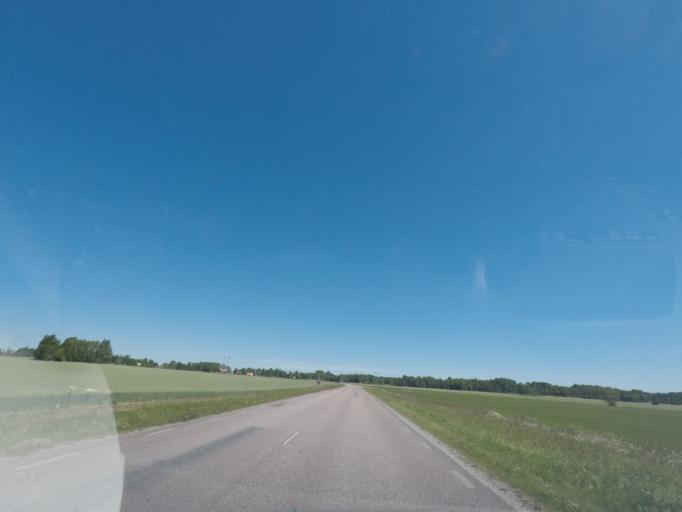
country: SE
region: Vaestmanland
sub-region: Vasteras
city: Tillberga
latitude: 59.6512
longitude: 16.6878
